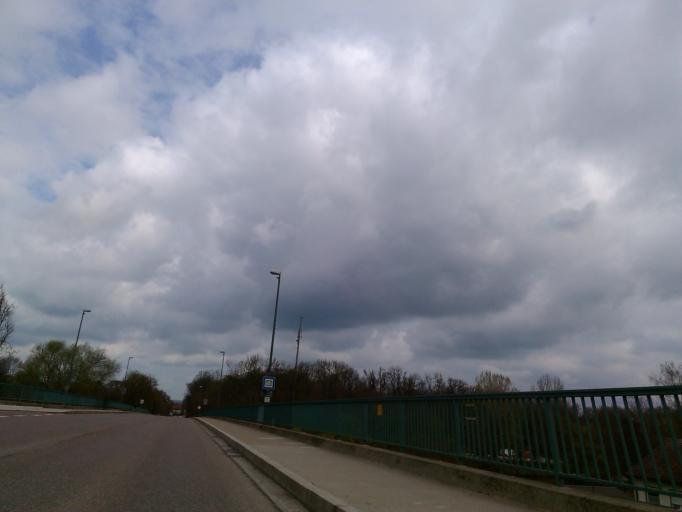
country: DE
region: Bavaria
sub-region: Swabia
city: Leipheim
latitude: 48.4505
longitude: 10.2161
